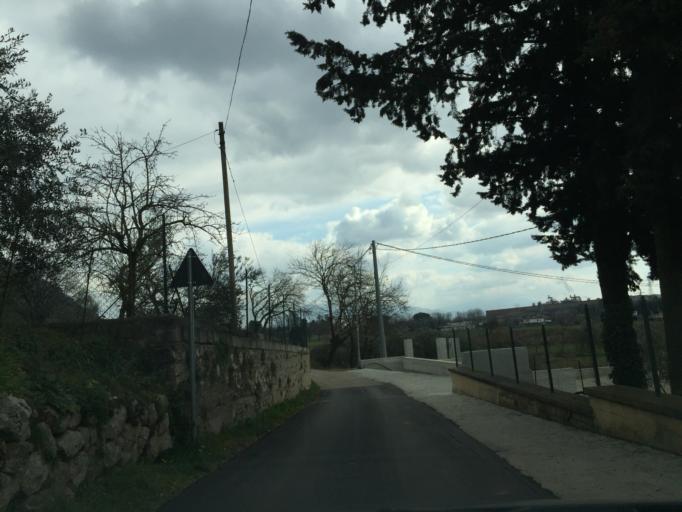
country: IT
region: Latium
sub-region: Provincia di Frosinone
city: Villa Santa Lucia
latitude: 41.4898
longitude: 13.7852
